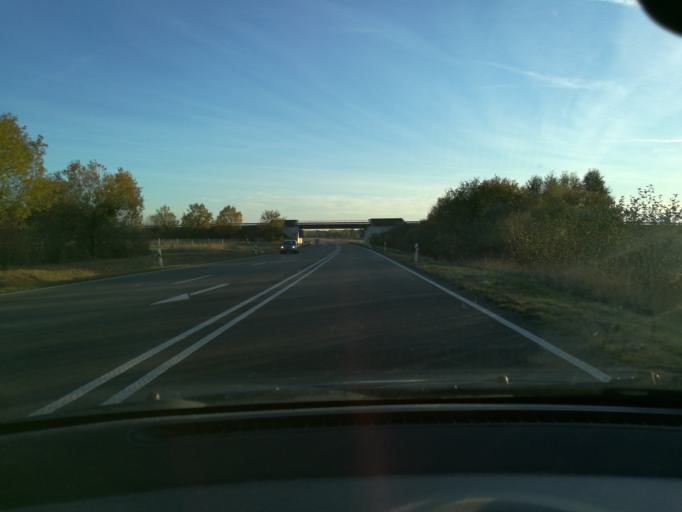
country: DE
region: Brandenburg
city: Perleberg
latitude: 53.0768
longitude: 11.8284
